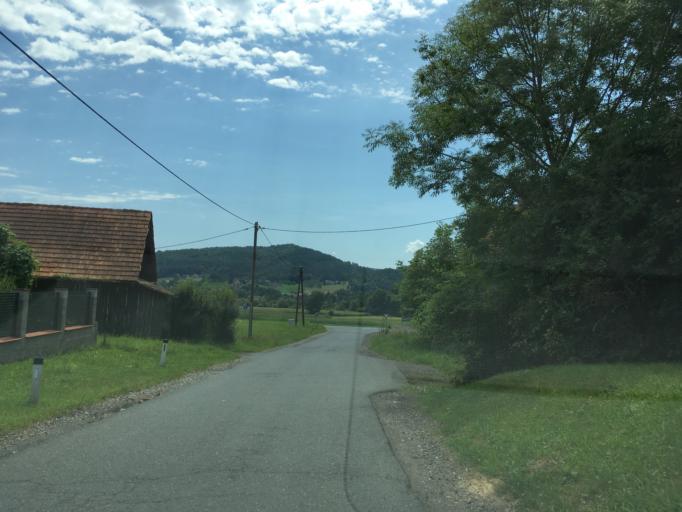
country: AT
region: Styria
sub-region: Politischer Bezirk Leibnitz
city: Gleinstatten
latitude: 46.7641
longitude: 15.3952
